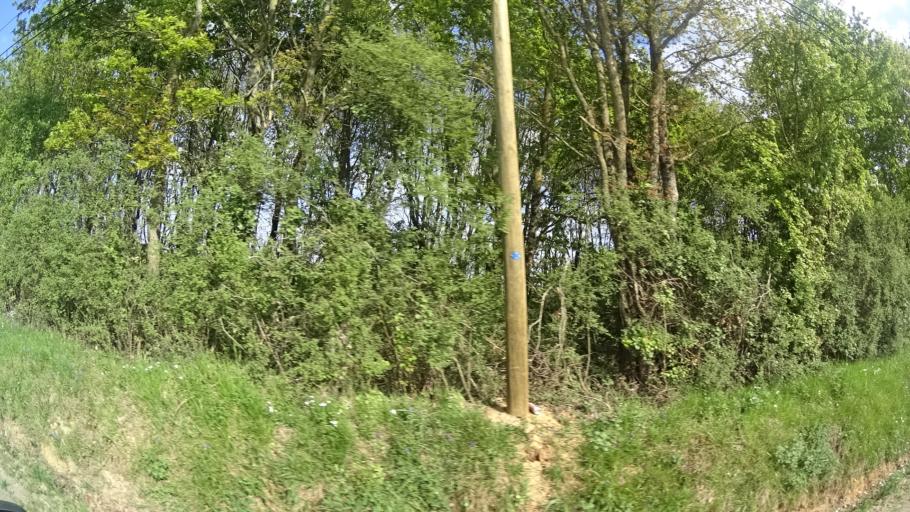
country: FR
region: Pays de la Loire
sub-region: Departement de la Loire-Atlantique
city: Saint-Nicolas-de-Redon
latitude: 47.6304
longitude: -2.0625
